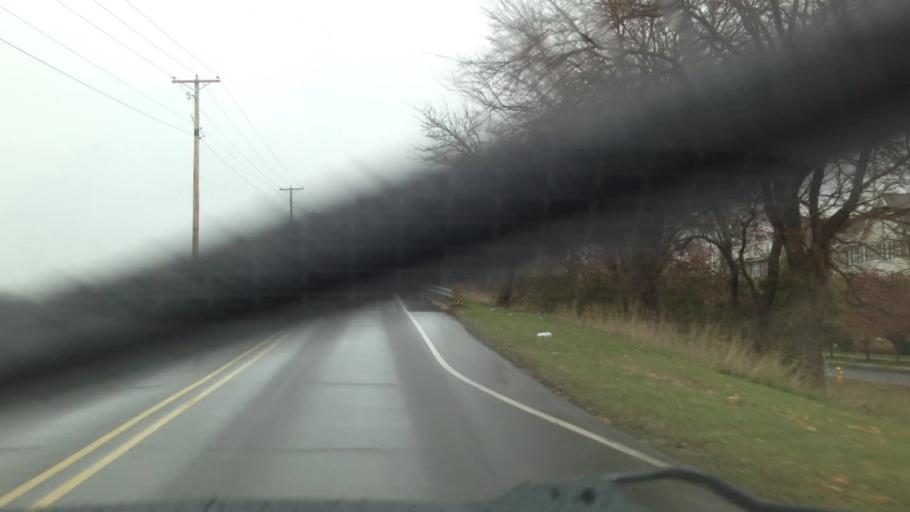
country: US
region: Indiana
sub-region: Saint Joseph County
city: Mishawaka
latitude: 41.7176
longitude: -86.1634
